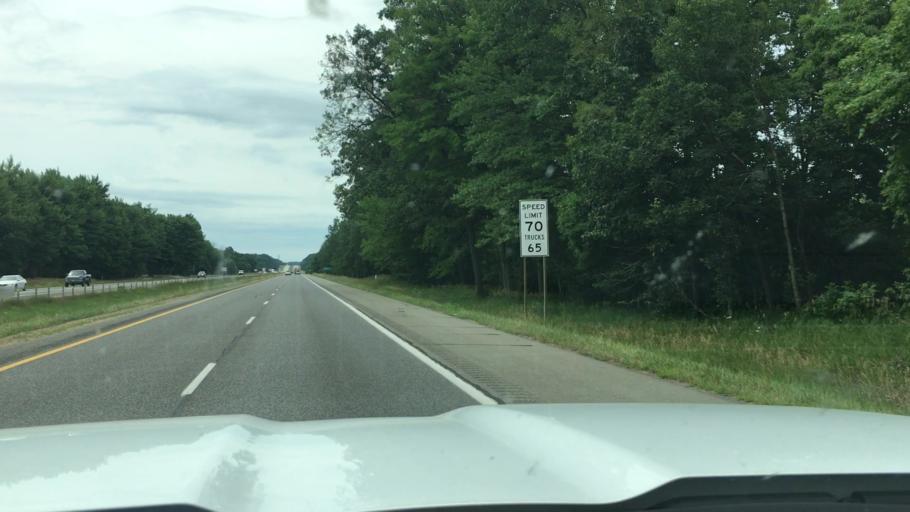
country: US
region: Michigan
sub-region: Allegan County
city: Otsego
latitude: 42.5286
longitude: -85.6586
